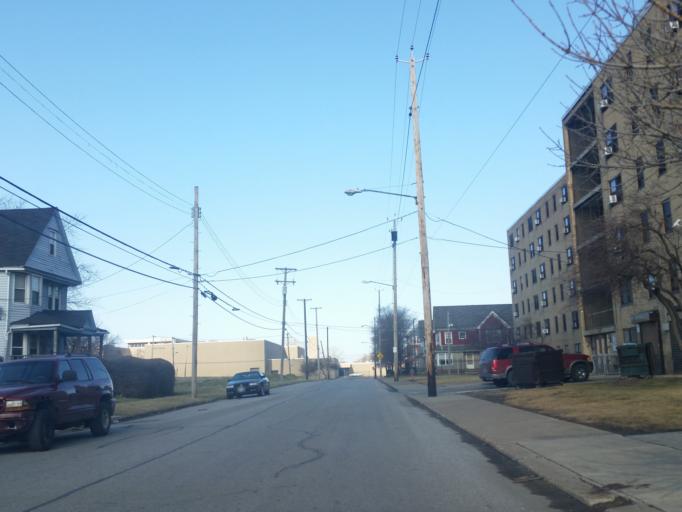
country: US
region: Ohio
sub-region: Cuyahoga County
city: Newburgh Heights
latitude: 41.4900
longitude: -81.6492
